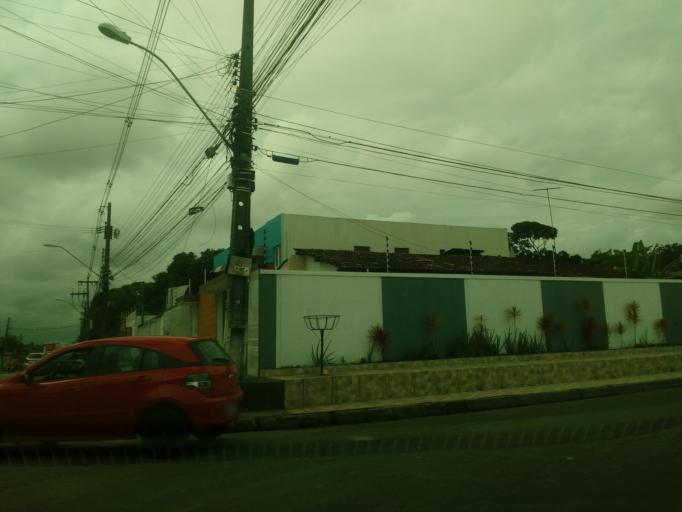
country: BR
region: Alagoas
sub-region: Satuba
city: Satuba
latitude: -9.5607
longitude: -35.7819
